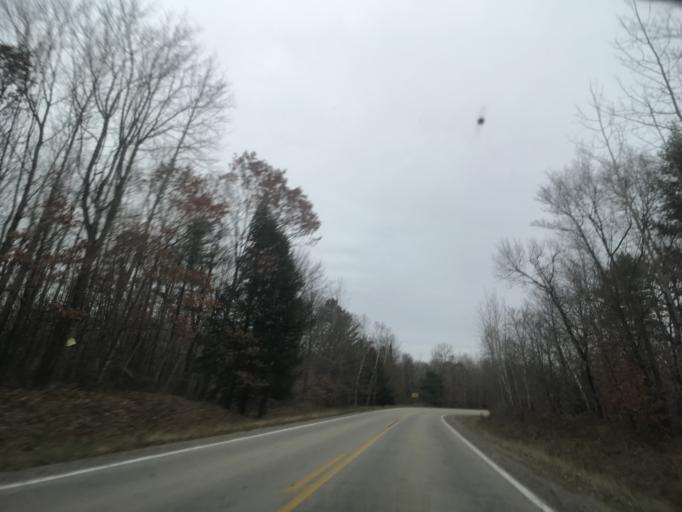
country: US
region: Wisconsin
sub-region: Menominee County
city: Legend Lake
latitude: 45.3197
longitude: -88.4615
